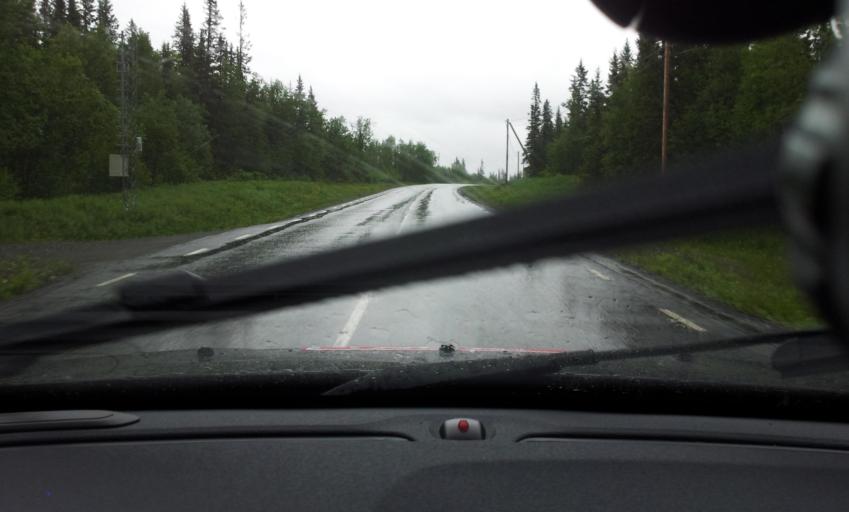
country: SE
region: Jaemtland
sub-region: Are Kommun
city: Are
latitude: 63.2612
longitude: 13.2147
